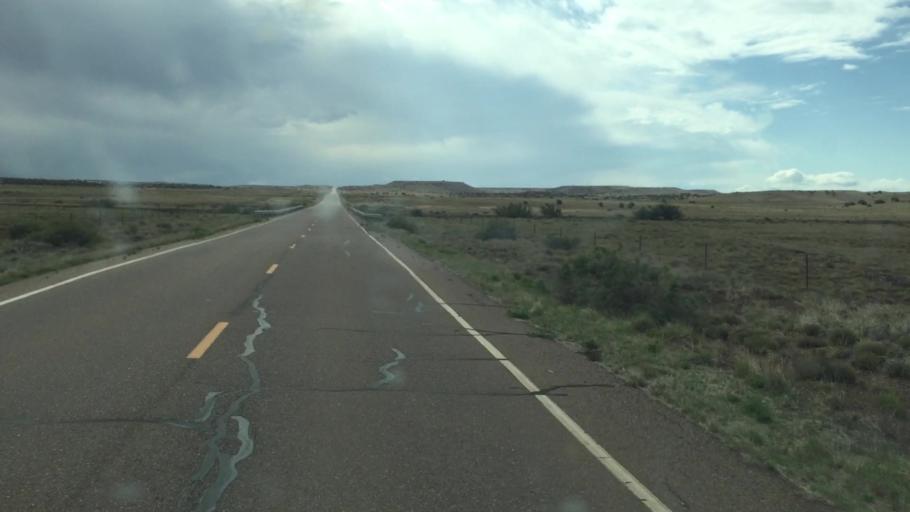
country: US
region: Arizona
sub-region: Apache County
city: Saint Johns
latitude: 34.5082
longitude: -109.6774
